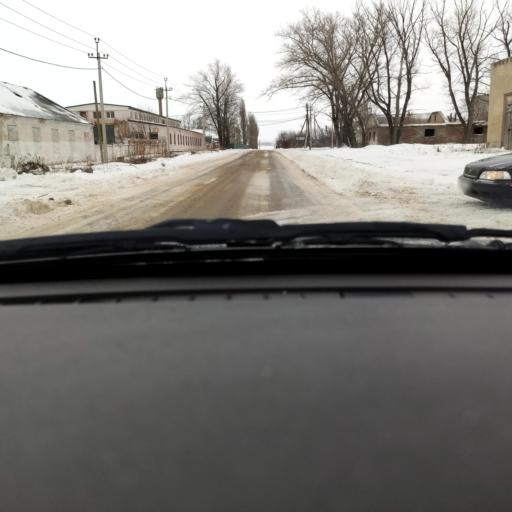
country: RU
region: Voronezj
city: Maslovka
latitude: 51.5375
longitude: 39.3425
